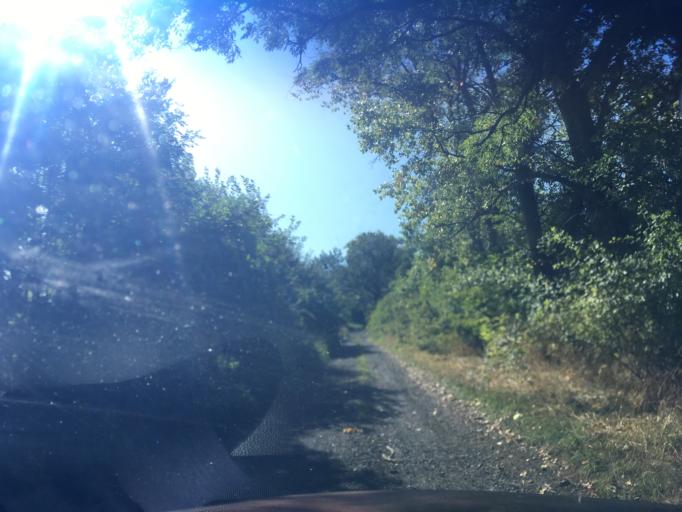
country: PL
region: Lower Silesian Voivodeship
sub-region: Powiat lubanski
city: Lesna
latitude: 51.0006
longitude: 15.1983
